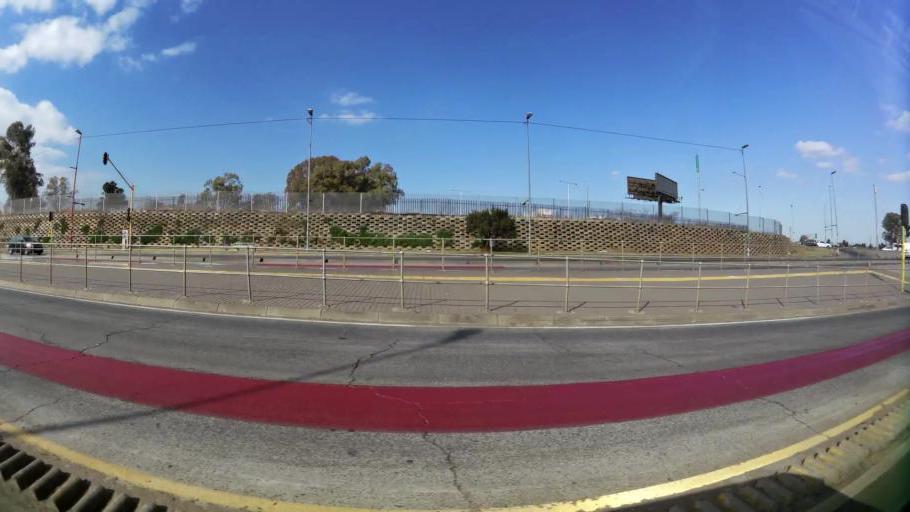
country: ZA
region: Gauteng
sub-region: City of Johannesburg Metropolitan Municipality
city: Soweto
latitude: -26.2614
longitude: 27.8904
